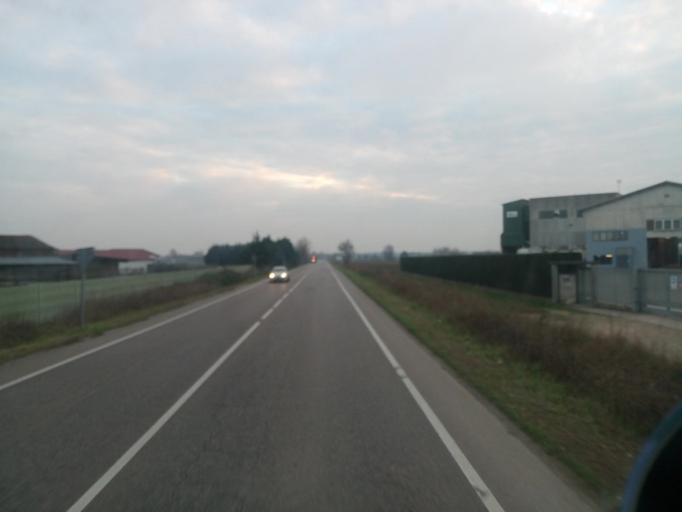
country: IT
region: Veneto
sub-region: Provincia di Verona
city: Pradelle
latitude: 45.2908
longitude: 10.8583
